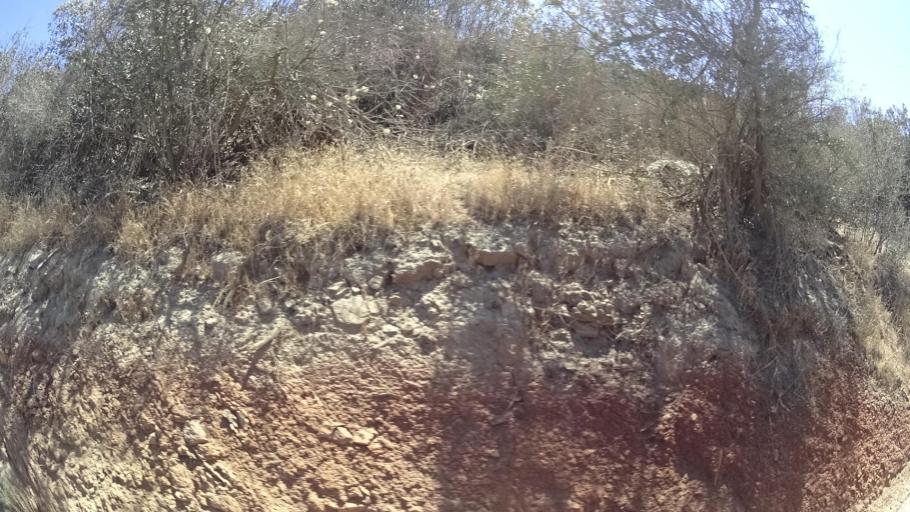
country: US
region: California
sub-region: San Diego County
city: Rainbow
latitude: 33.3569
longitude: -117.0651
